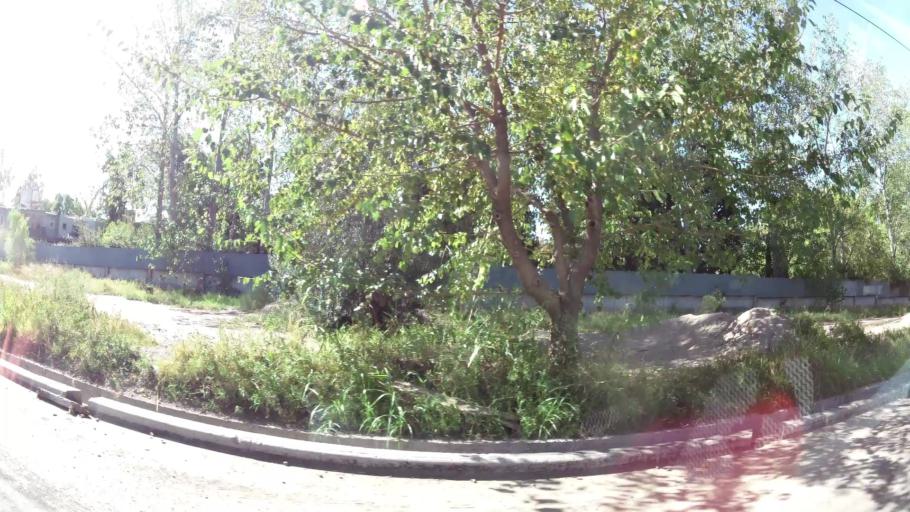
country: AR
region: Mendoza
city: Villa Nueva
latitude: -32.9106
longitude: -68.7903
